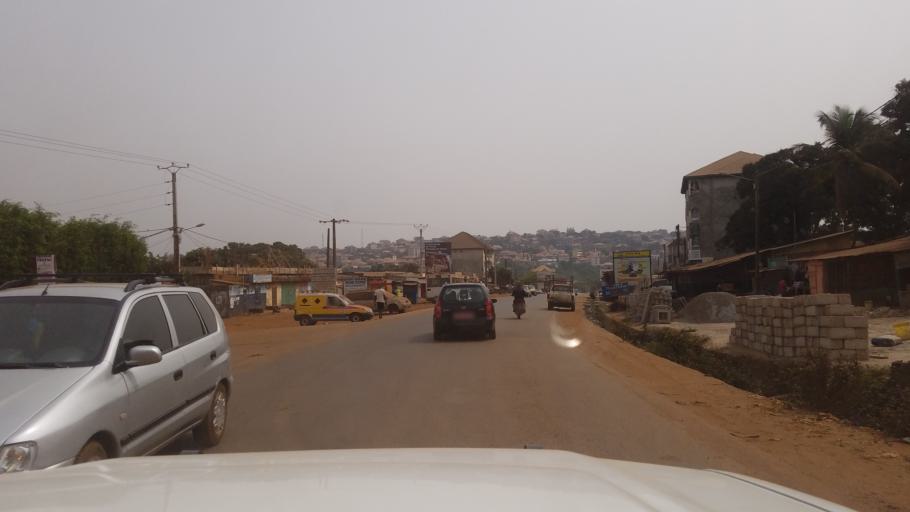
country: GN
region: Conakry
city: Conakry
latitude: 9.6459
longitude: -13.6082
